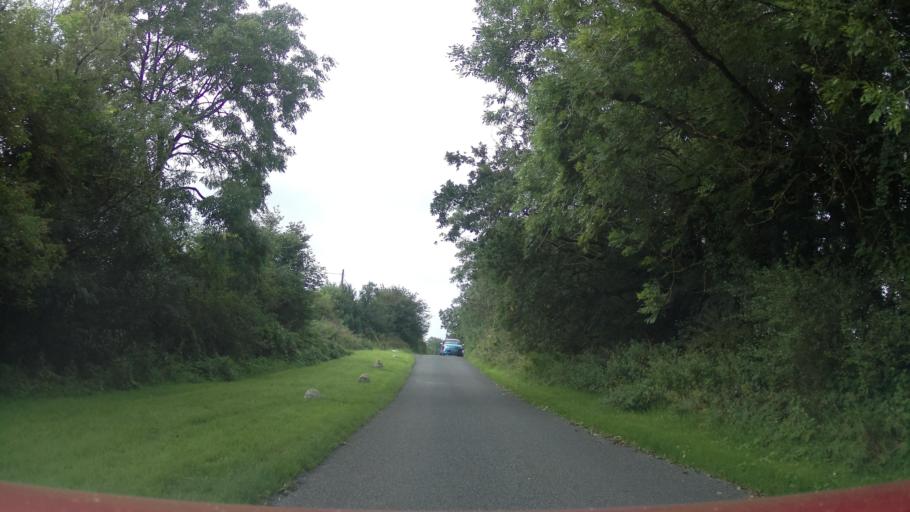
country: GB
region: England
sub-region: Somerset
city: Shepton Mallet
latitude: 51.2108
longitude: -2.5017
